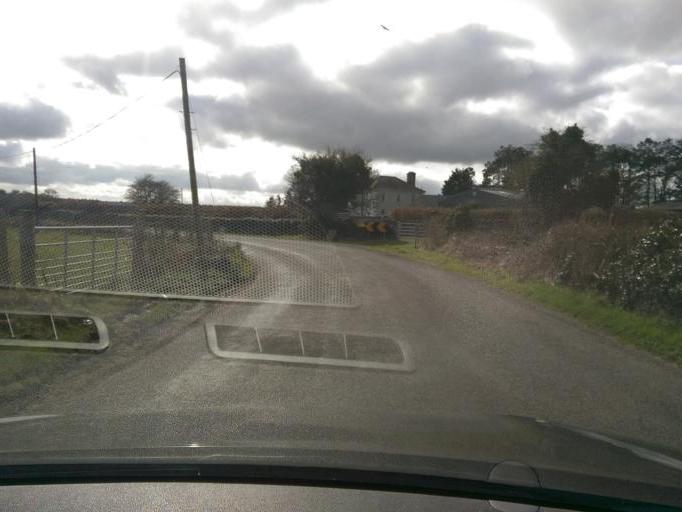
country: IE
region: Connaught
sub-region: County Galway
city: Ballinasloe
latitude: 53.3489
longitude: -8.3901
